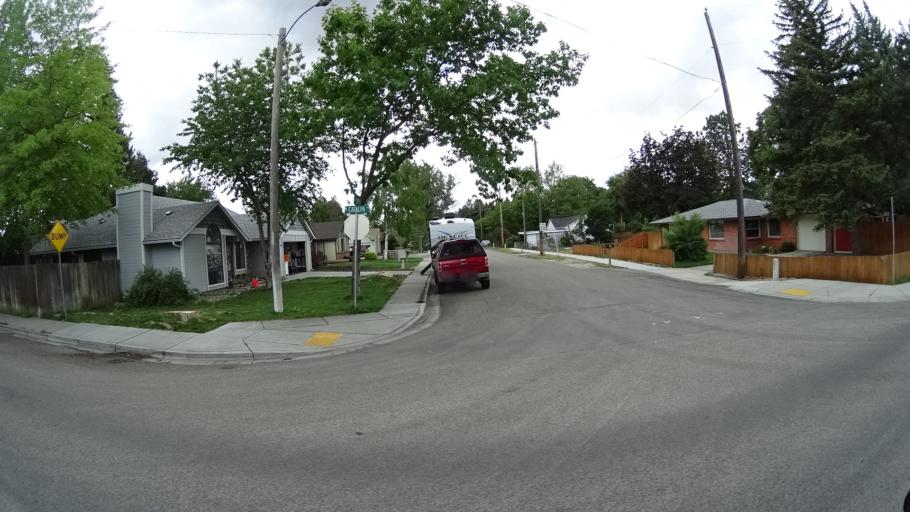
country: US
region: Idaho
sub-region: Ada County
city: Garden City
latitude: 43.6555
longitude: -116.2369
